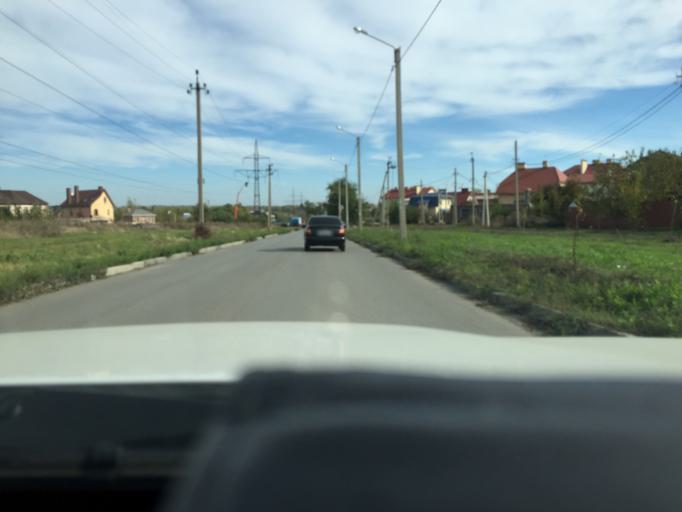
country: RU
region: Rostov
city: Aksay
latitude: 47.2999
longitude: 39.8168
